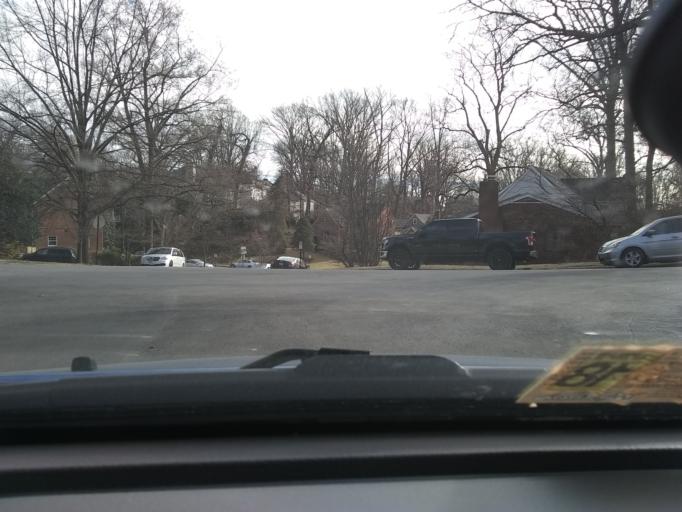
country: US
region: Virginia
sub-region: Fairfax County
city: Seven Corners
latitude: 38.8869
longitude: -77.1330
